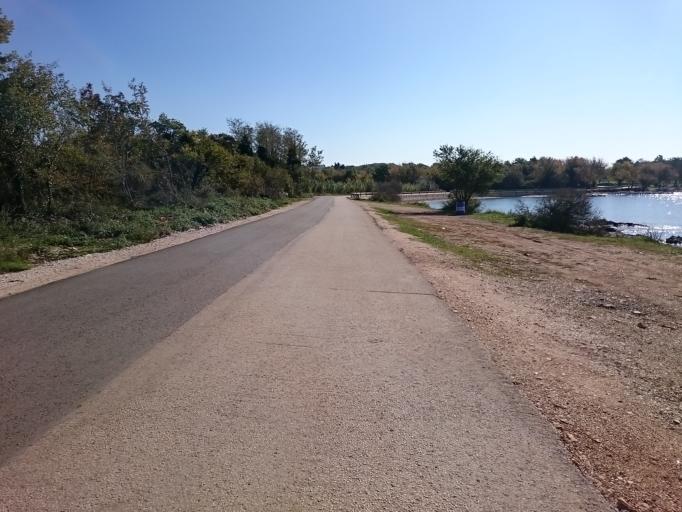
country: HR
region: Istarska
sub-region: Grad Porec
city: Porec
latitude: 45.2547
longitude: 13.5948
